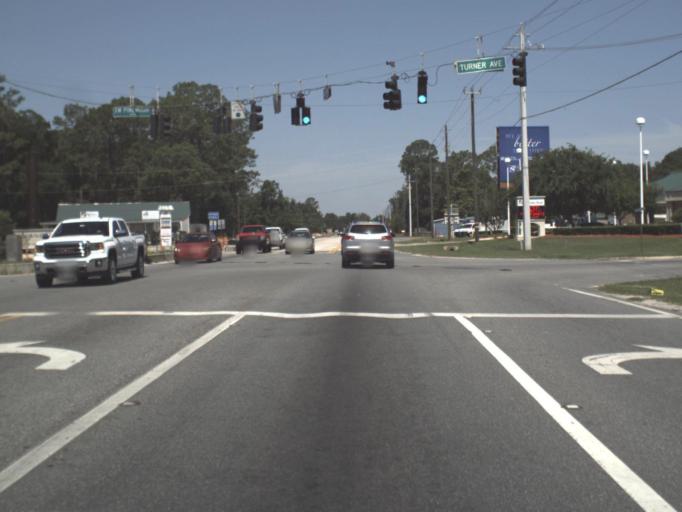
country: US
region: Florida
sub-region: Columbia County
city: Lake City
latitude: 30.1845
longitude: -82.7093
